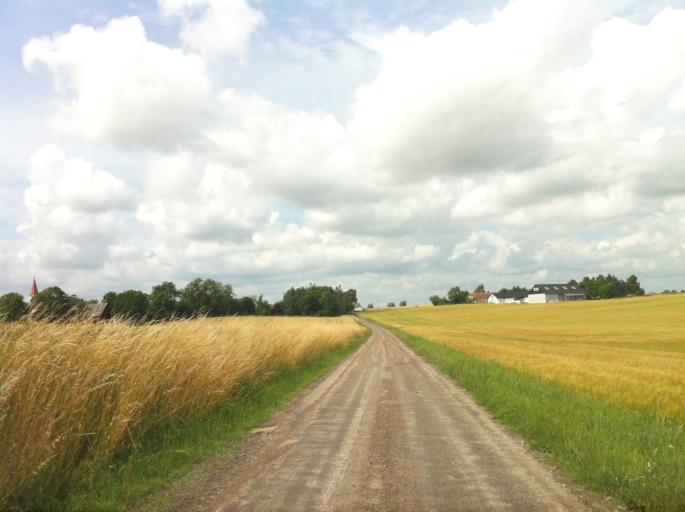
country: SE
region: Skane
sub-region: Skurups Kommun
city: Skurup
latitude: 55.4089
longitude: 13.4630
